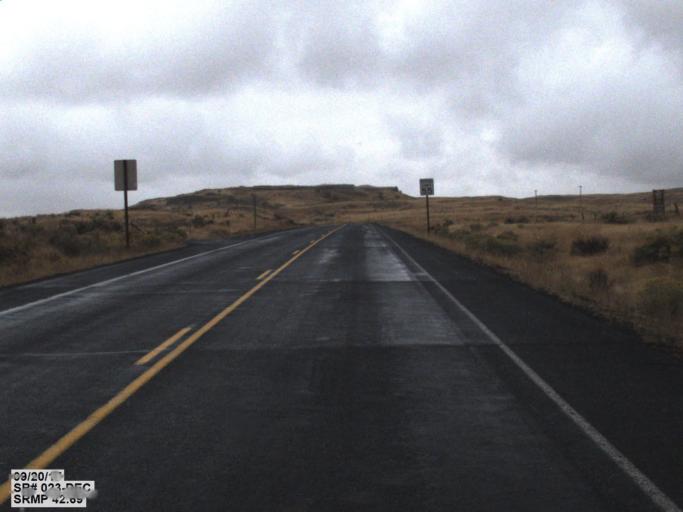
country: US
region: Washington
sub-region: Lincoln County
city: Davenport
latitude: 47.2939
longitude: -117.9727
